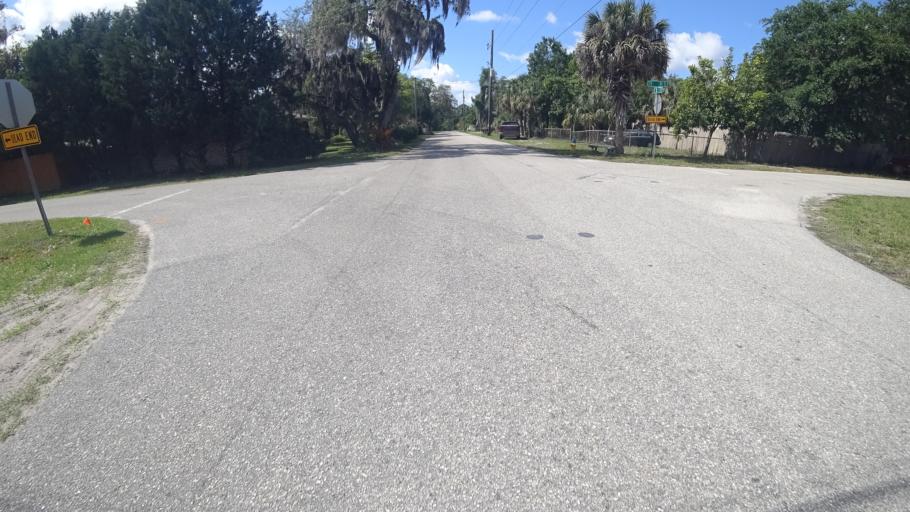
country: US
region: Florida
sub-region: Manatee County
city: Whitfield
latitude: 27.4133
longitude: -82.5289
